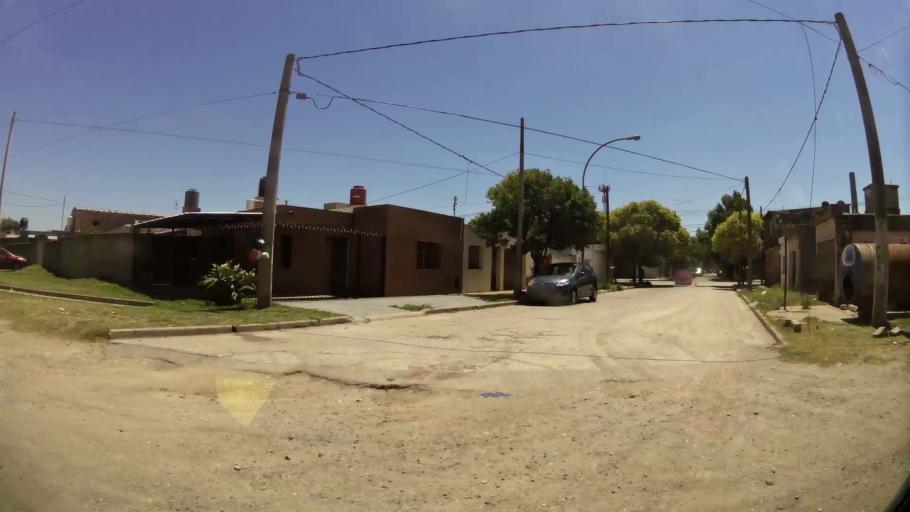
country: AR
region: Cordoba
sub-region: Departamento de Capital
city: Cordoba
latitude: -31.3858
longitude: -64.1479
